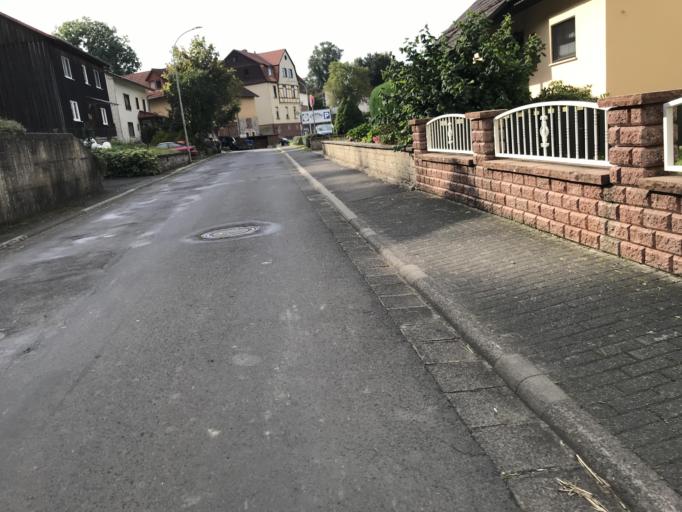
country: DE
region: Hesse
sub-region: Regierungsbezirk Giessen
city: Alsfeld
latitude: 50.7334
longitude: 9.2739
